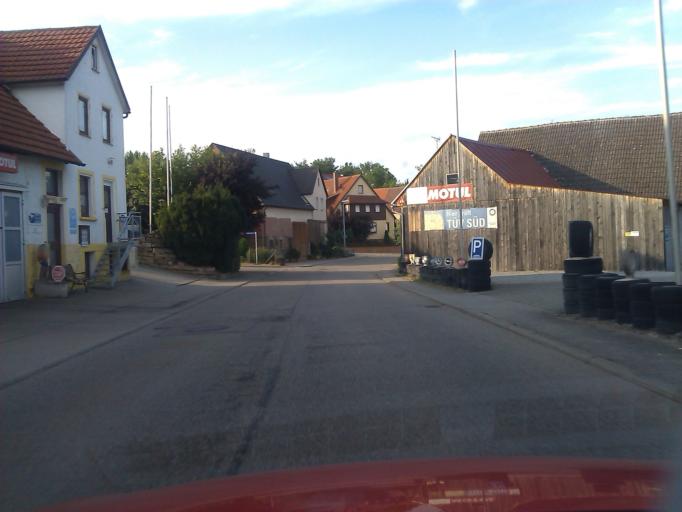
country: DE
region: Baden-Wuerttemberg
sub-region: Regierungsbezirk Stuttgart
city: Pfaffenhofen
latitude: 49.1093
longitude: 8.9821
